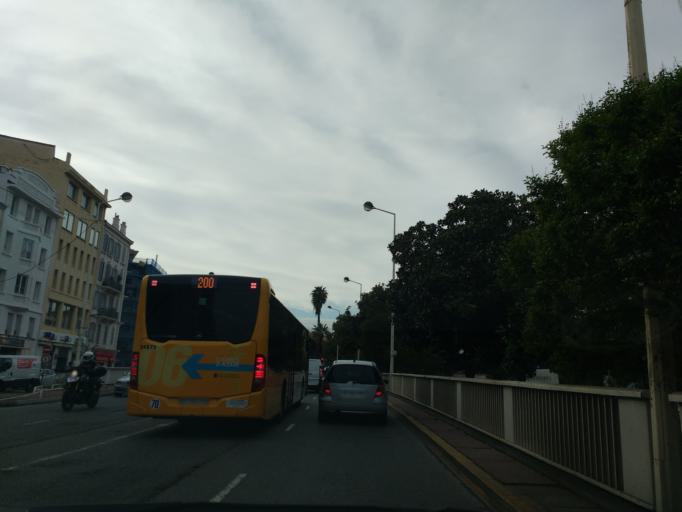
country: FR
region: Provence-Alpes-Cote d'Azur
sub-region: Departement des Alpes-Maritimes
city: Cannes
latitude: 43.5523
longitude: 7.0290
